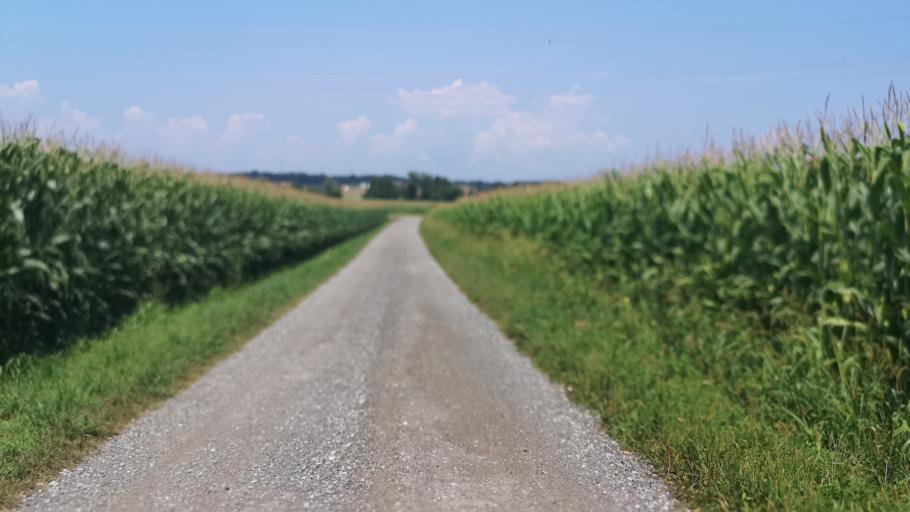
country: AT
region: Styria
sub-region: Politischer Bezirk Deutschlandsberg
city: Wettmannstatten
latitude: 46.8272
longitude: 15.3692
